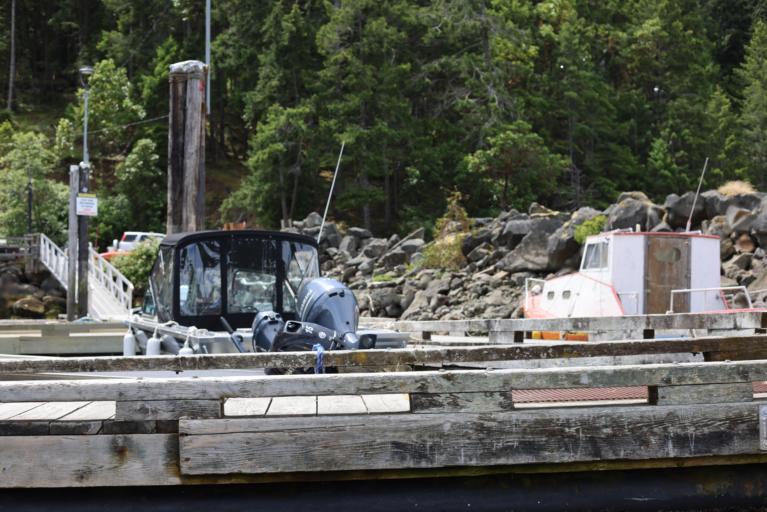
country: CA
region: British Columbia
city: Nanaimo
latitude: 49.1371
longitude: -123.8073
